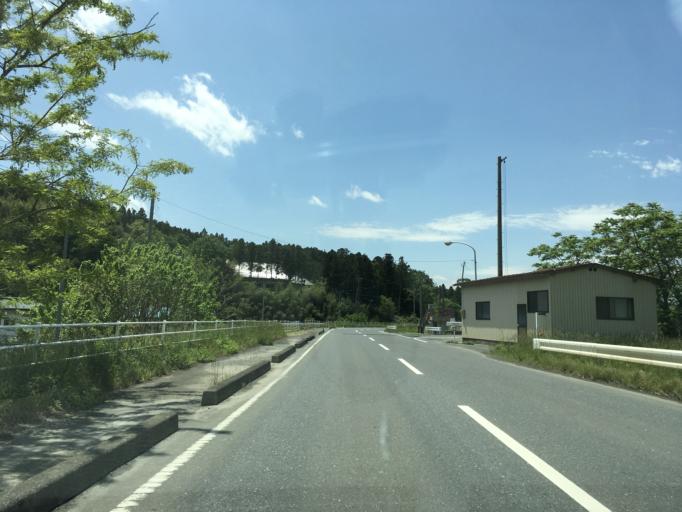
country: JP
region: Miyagi
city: Wakuya
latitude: 38.6570
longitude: 141.3072
